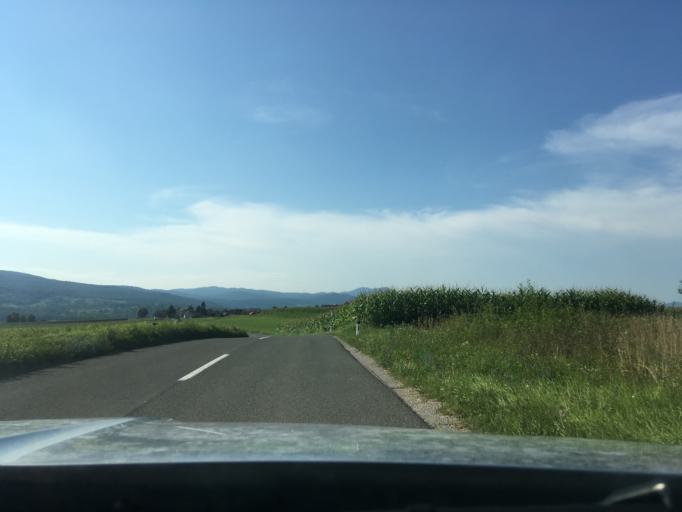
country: SI
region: Crnomelj
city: Crnomelj
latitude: 45.5146
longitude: 15.1830
